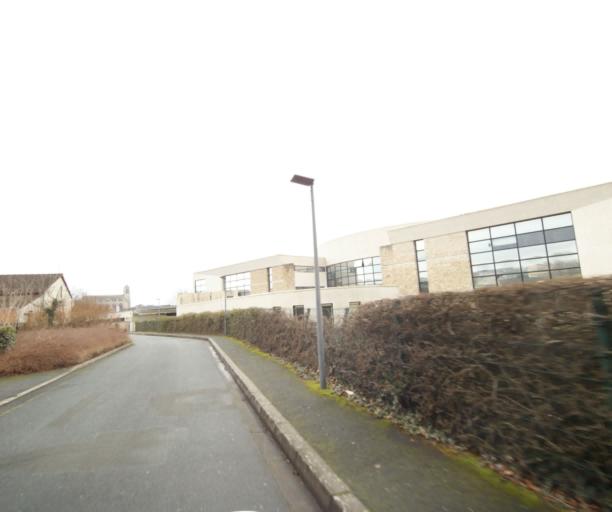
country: FR
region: Poitou-Charentes
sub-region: Departement des Deux-Sevres
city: Niort
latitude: 46.3322
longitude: -0.4687
